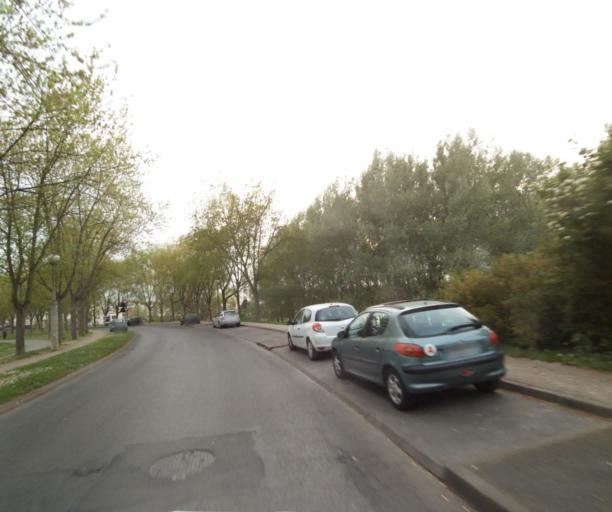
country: FR
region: Ile-de-France
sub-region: Departement de Seine-et-Marne
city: Torcy
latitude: 48.8438
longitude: 2.6410
